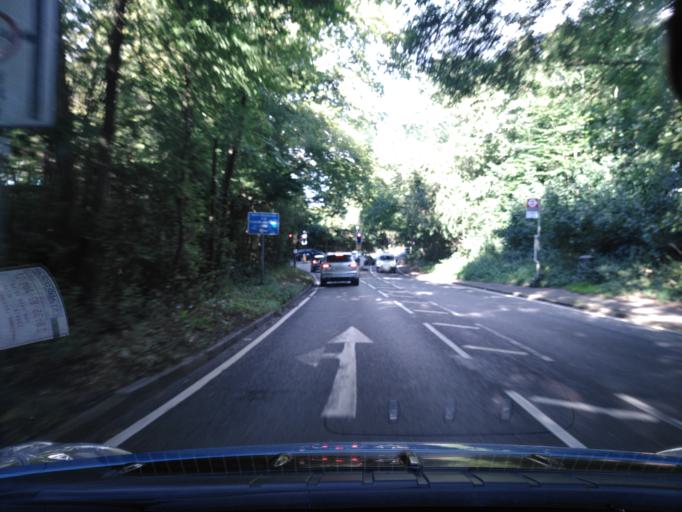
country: GB
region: England
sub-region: Greater London
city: Hendon
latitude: 51.6302
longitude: -0.2369
